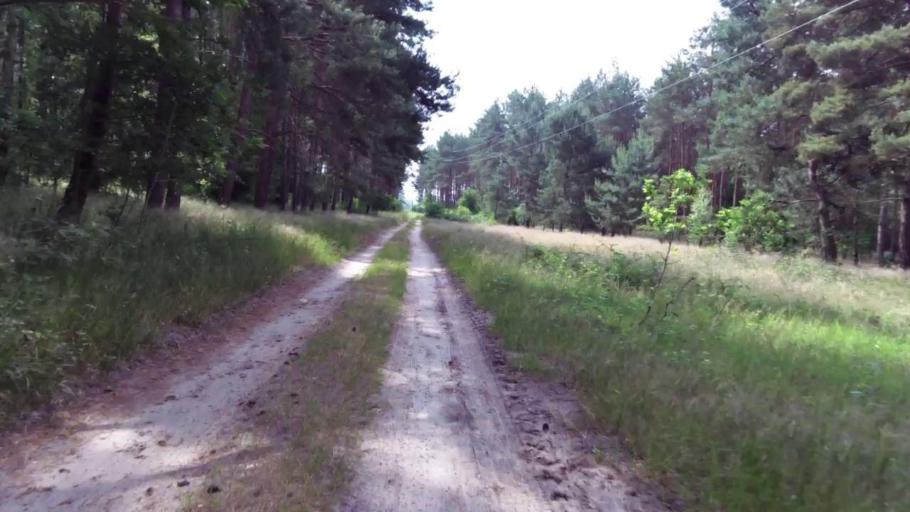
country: PL
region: West Pomeranian Voivodeship
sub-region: Powiat kamienski
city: Wolin
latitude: 53.7694
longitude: 14.6443
